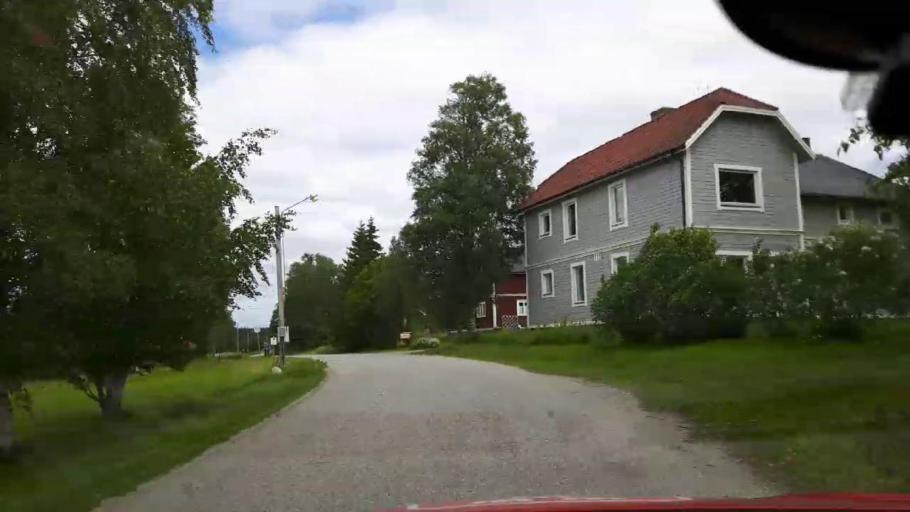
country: SE
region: Jaemtland
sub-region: Braecke Kommun
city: Braecke
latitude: 62.8735
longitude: 15.2725
